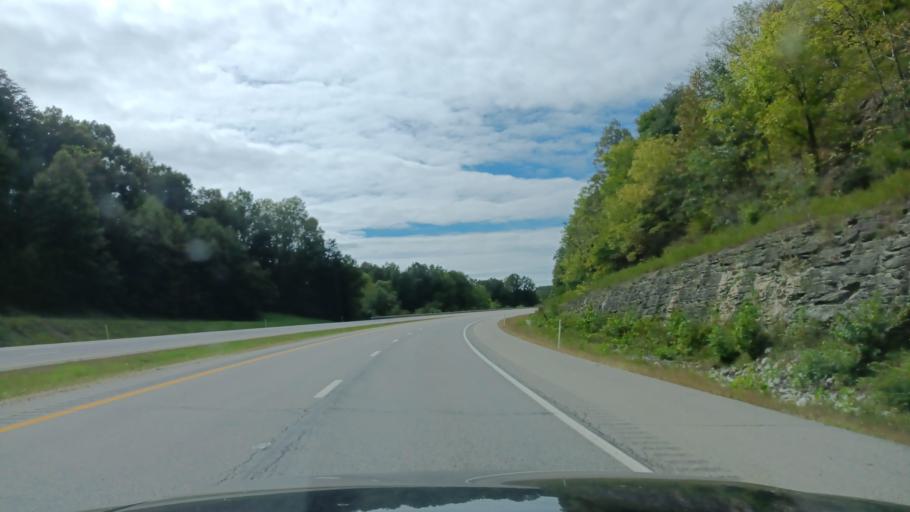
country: US
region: West Virginia
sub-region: Ritchie County
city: Pennsboro
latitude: 39.2655
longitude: -80.9227
